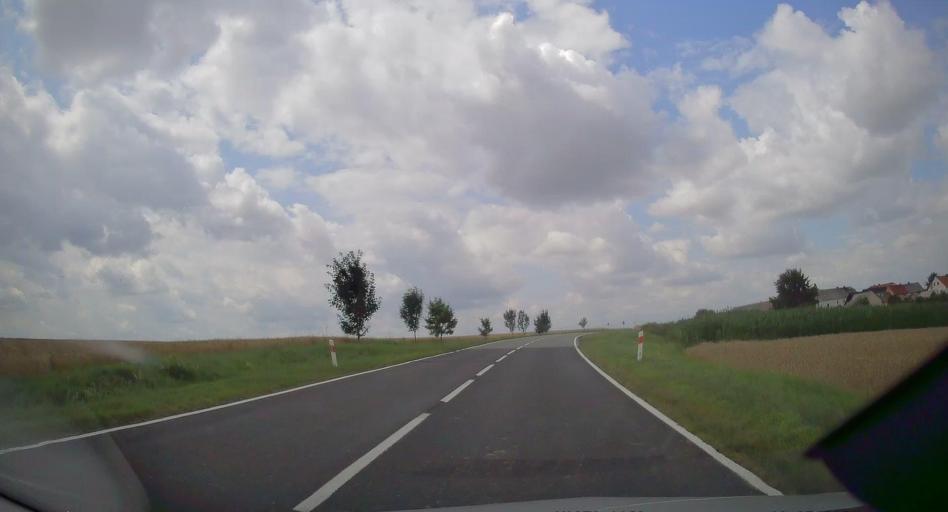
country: PL
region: Opole Voivodeship
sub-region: Powiat prudnicki
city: Raclawice Slaskie
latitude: 50.3494
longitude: 17.7794
